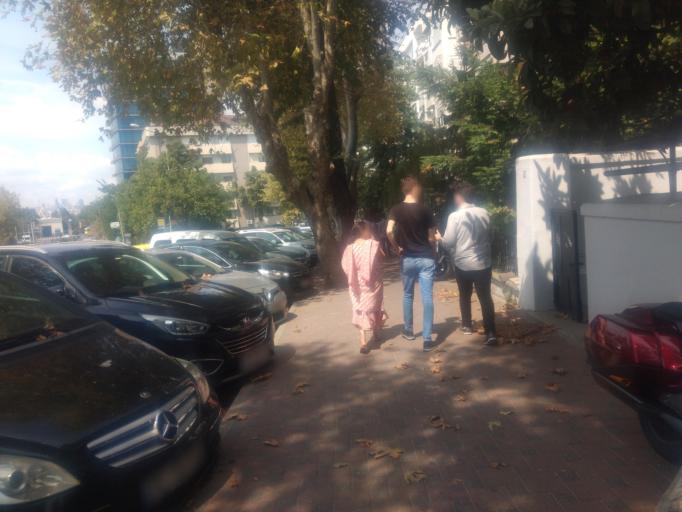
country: TR
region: Istanbul
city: UEskuedar
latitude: 40.9869
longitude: 29.0217
